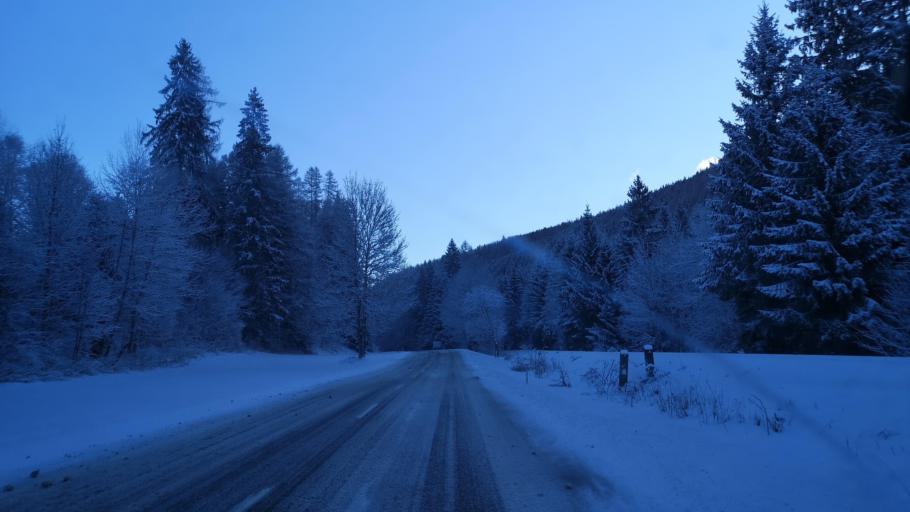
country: SK
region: Banskobystricky
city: Revuca
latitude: 48.8284
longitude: 20.0932
